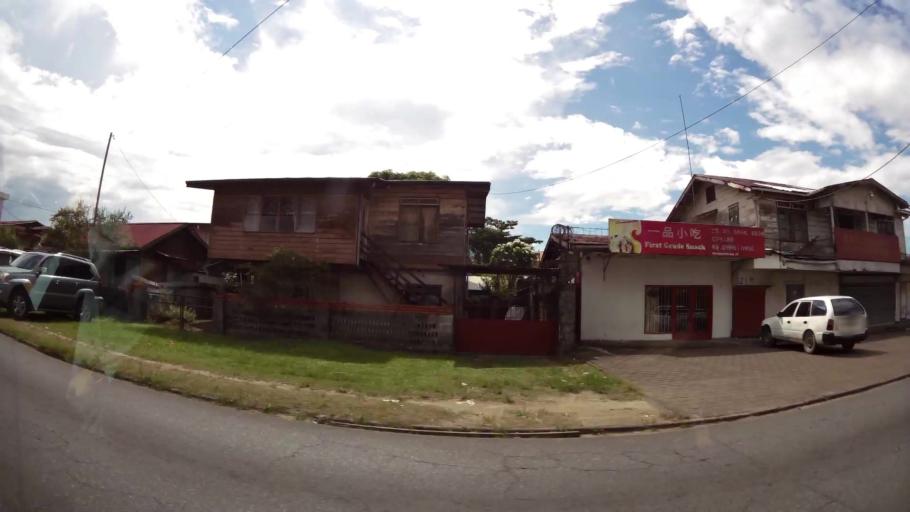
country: SR
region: Paramaribo
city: Paramaribo
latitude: 5.8379
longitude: -55.1463
